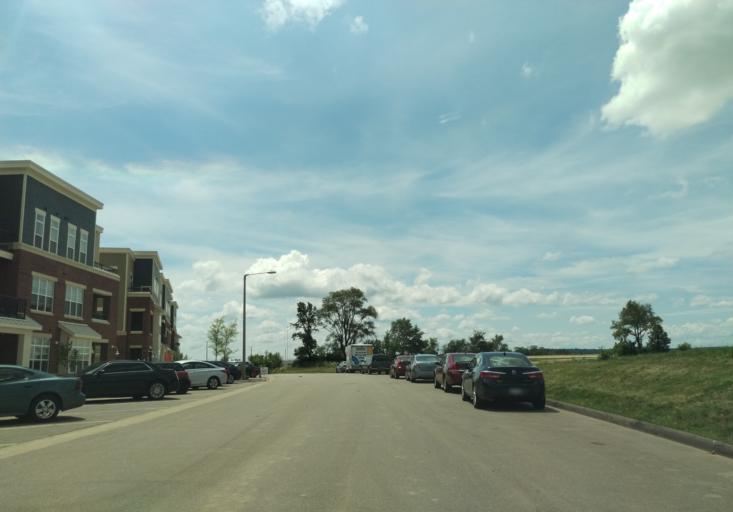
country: US
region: Wisconsin
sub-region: Dane County
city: Middleton
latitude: 43.1163
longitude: -89.5143
